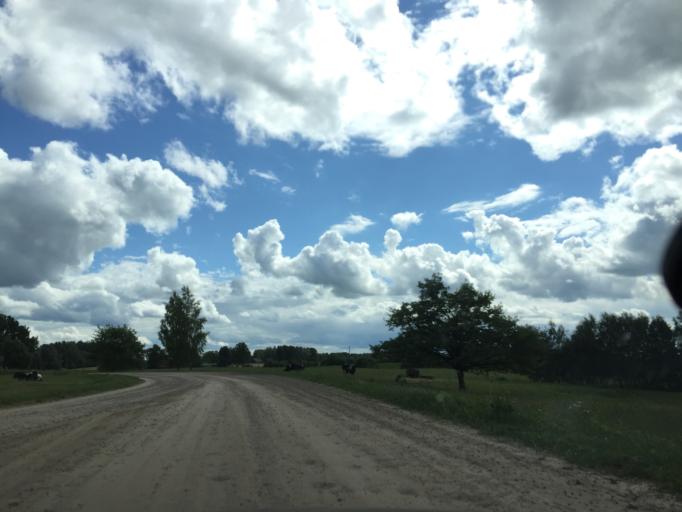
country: LV
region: Vecumnieki
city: Vecumnieki
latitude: 56.4226
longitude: 24.4977
